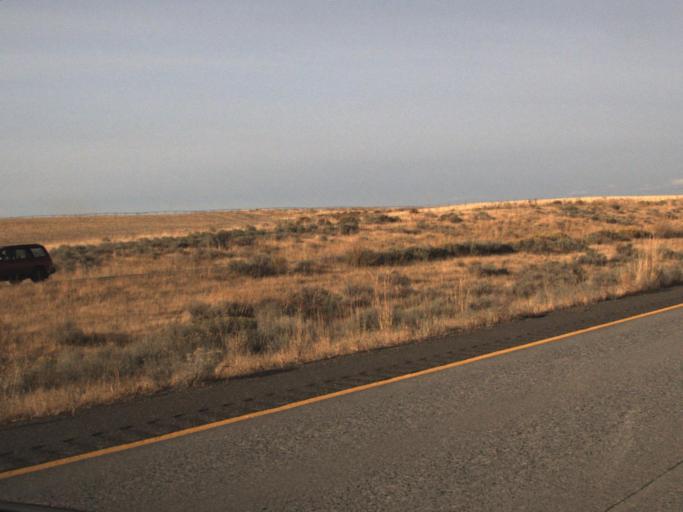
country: US
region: Oregon
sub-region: Umatilla County
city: Umatilla
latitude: 46.0078
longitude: -119.2405
